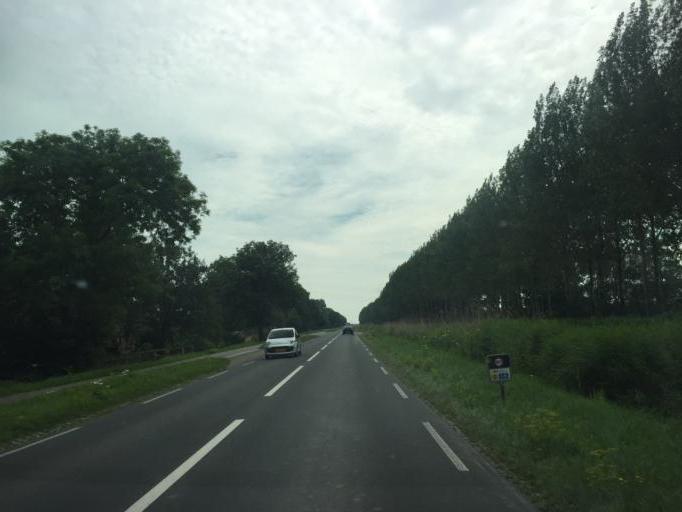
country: NL
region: North Holland
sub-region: Gemeente Heerhugowaard
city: Heerhugowaard
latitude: 52.6069
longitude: 4.8434
